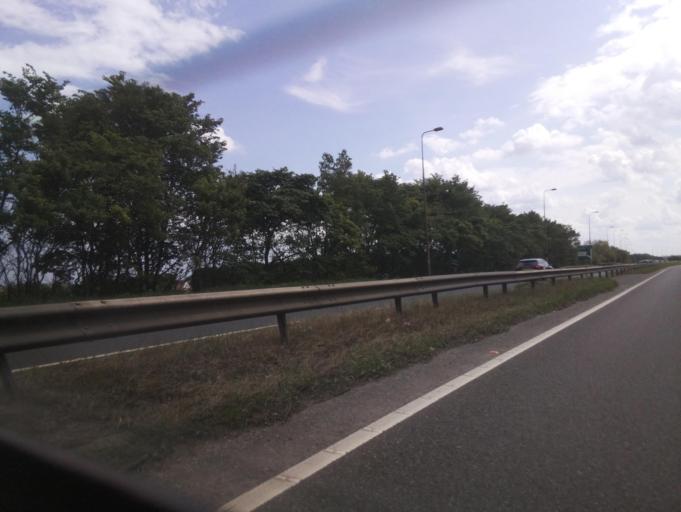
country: GB
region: England
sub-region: County Durham
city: Shotton
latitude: 54.7712
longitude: -1.3576
